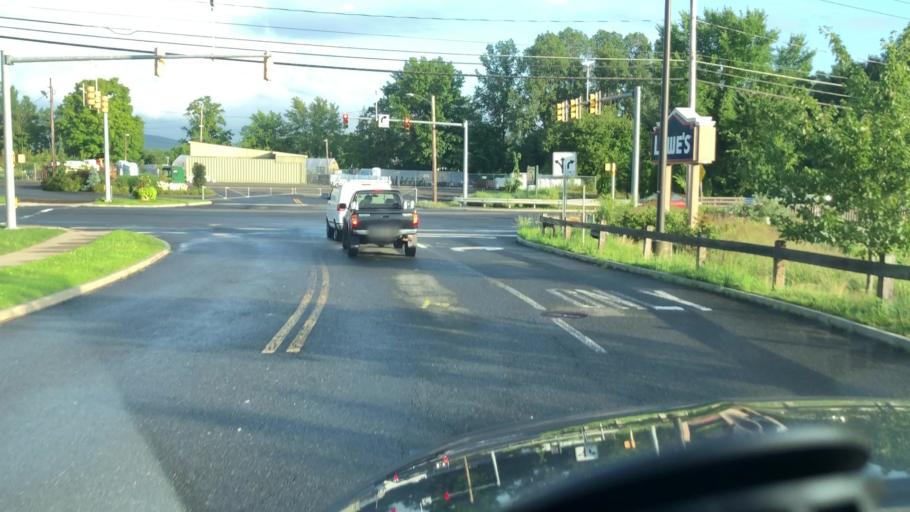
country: US
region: Massachusetts
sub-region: Hampshire County
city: Hadley
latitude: 42.3516
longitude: -72.5643
